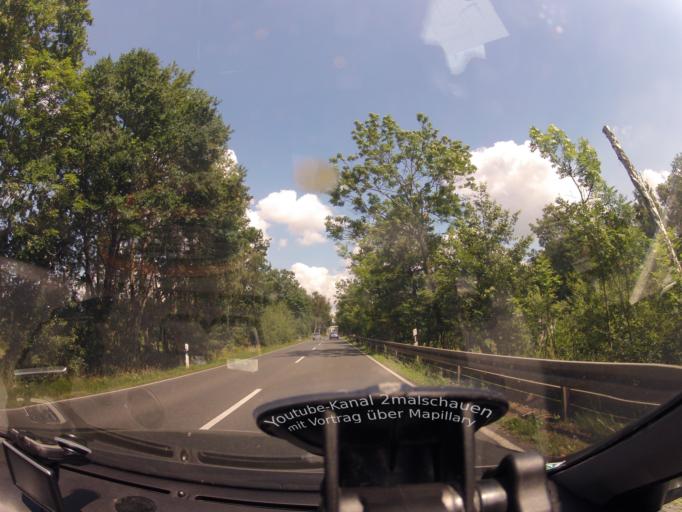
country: DE
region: Saxony
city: Zinna
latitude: 51.5480
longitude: 12.9584
